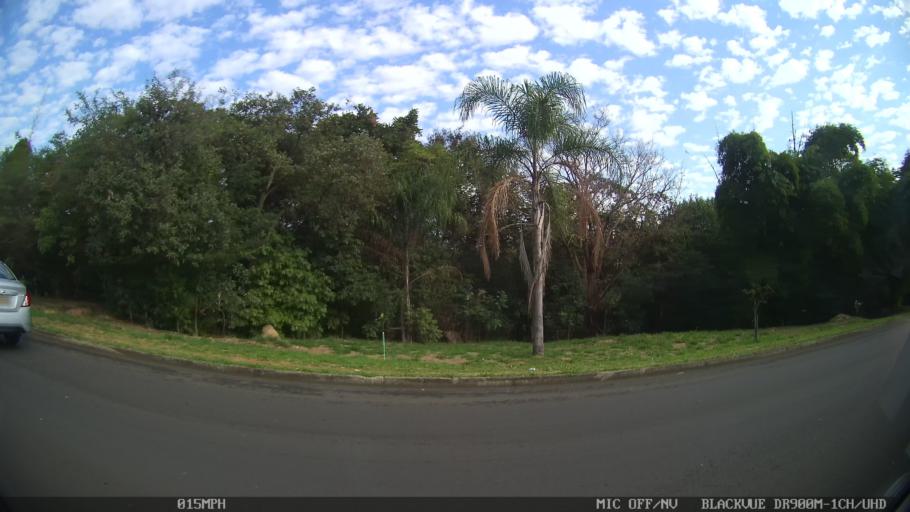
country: BR
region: Sao Paulo
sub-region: Americana
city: Americana
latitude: -22.7370
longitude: -47.3464
